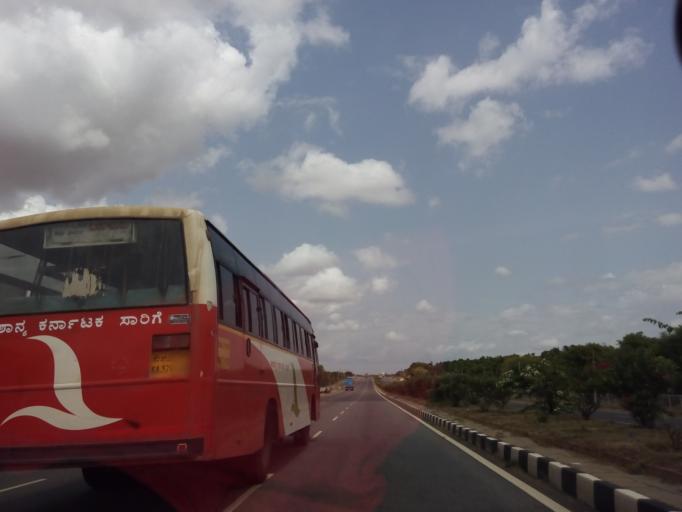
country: IN
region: Karnataka
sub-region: Tumkur
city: Sira
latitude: 13.8098
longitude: 76.7903
